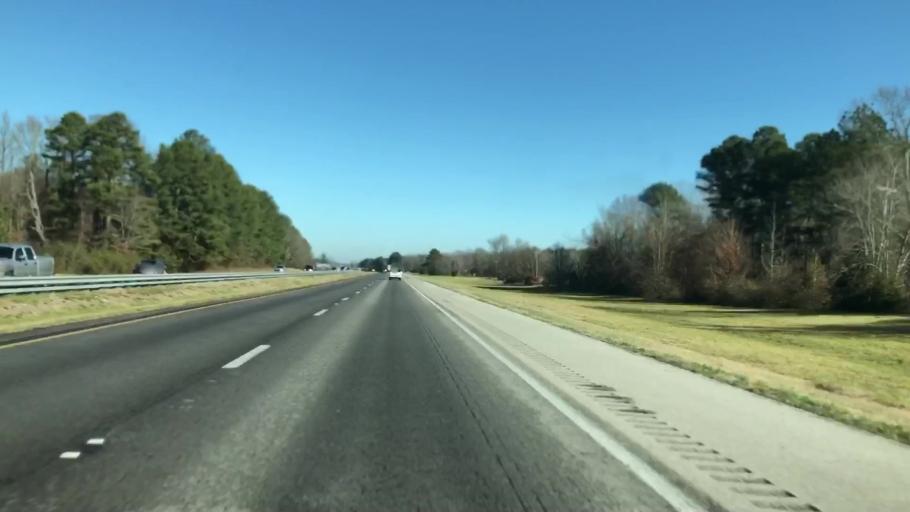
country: US
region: Alabama
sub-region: Limestone County
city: Athens
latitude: 34.8499
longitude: -86.9305
